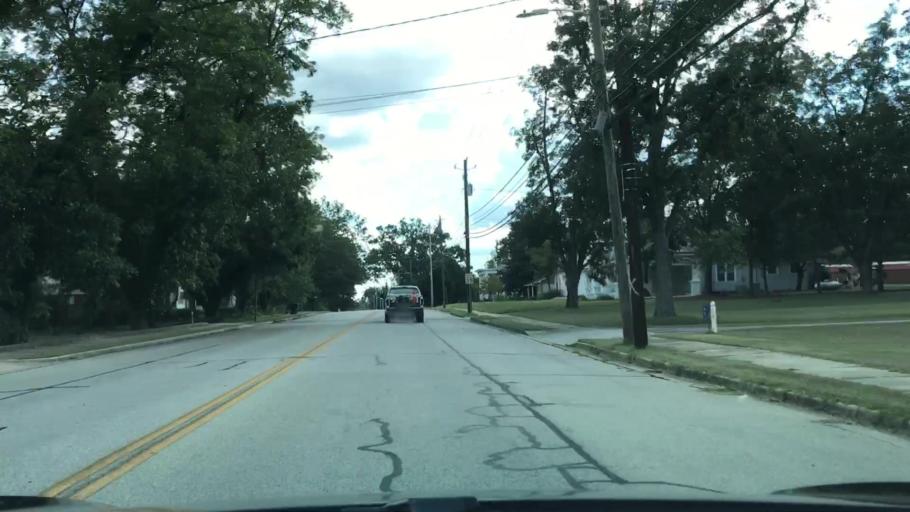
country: US
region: Georgia
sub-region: Jefferson County
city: Wadley
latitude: 32.8709
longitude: -82.4044
